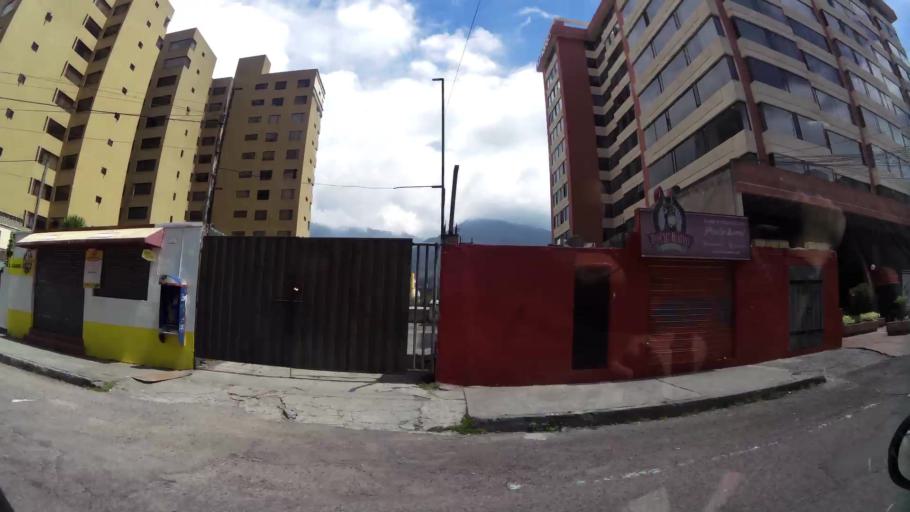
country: EC
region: Pichincha
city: Quito
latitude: -0.1793
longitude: -78.4870
